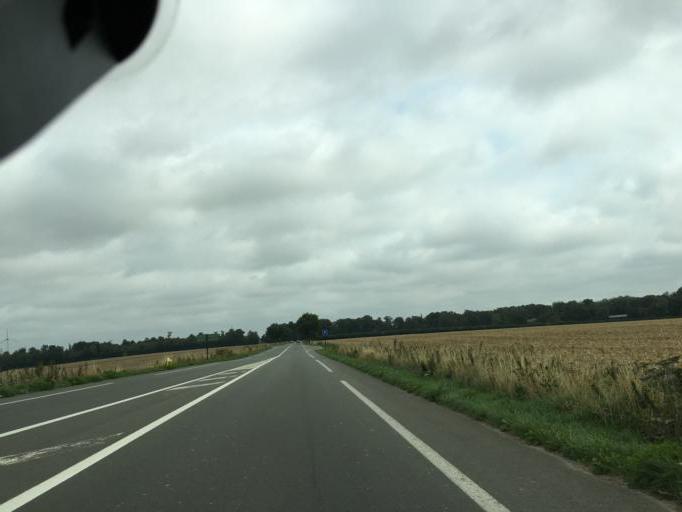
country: FR
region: Nord-Pas-de-Calais
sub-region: Departement du Pas-de-Calais
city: Saint-Pol-sur-Ternoise
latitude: 50.4062
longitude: 2.3660
